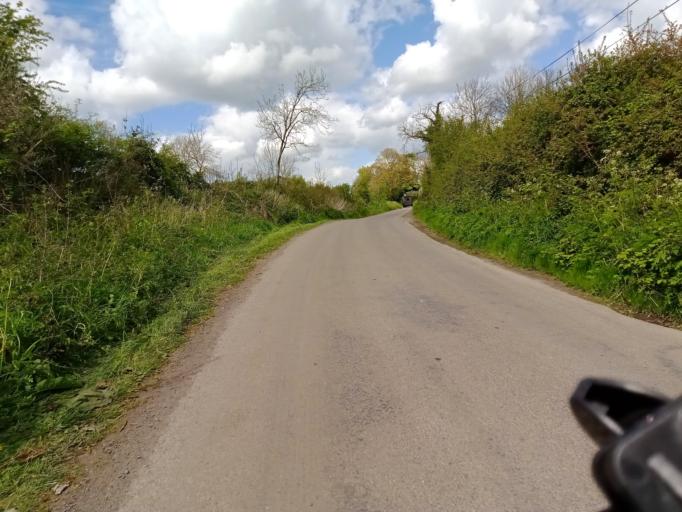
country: IE
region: Leinster
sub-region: Kilkenny
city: Thomastown
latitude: 52.5872
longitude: -7.1445
